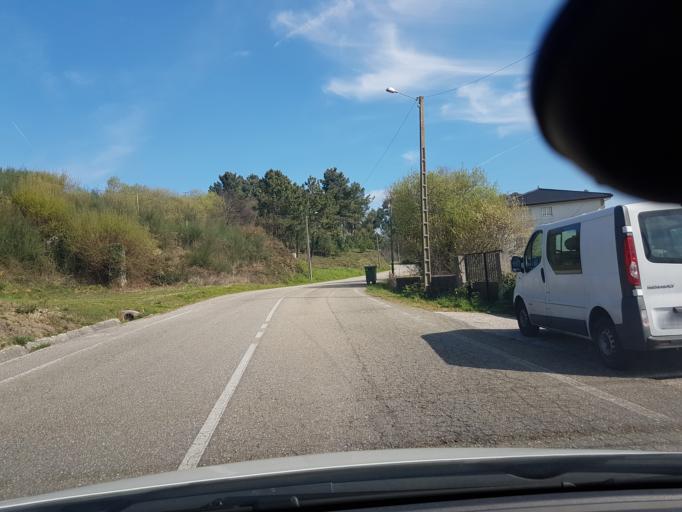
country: ES
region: Galicia
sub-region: Provincia de Pontevedra
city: Porrino
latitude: 42.2162
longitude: -8.6378
